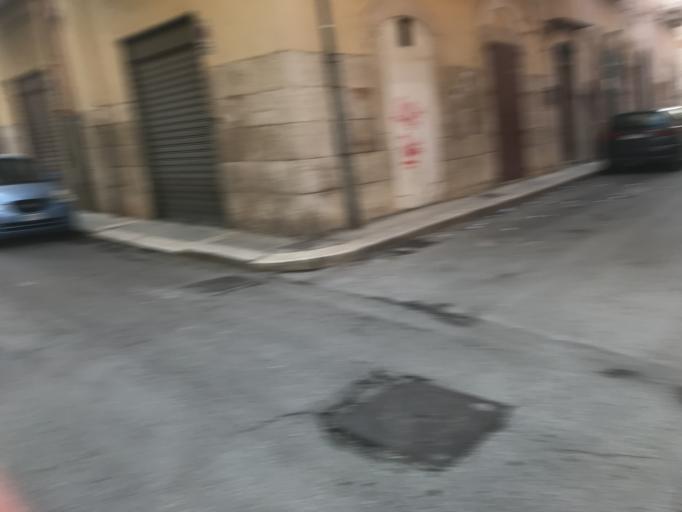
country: IT
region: Apulia
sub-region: Provincia di Bari
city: Corato
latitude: 41.1507
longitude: 16.4171
